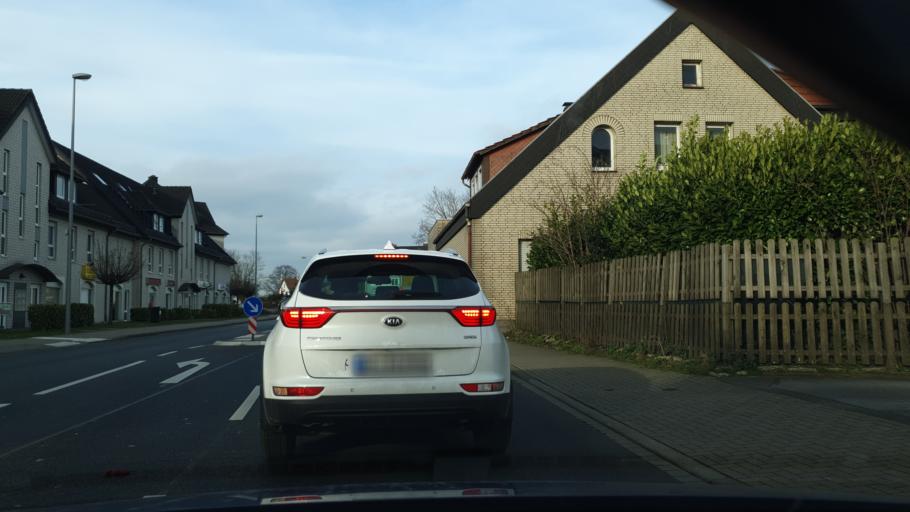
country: DE
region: North Rhine-Westphalia
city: Spenge
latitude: 52.0965
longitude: 8.5138
